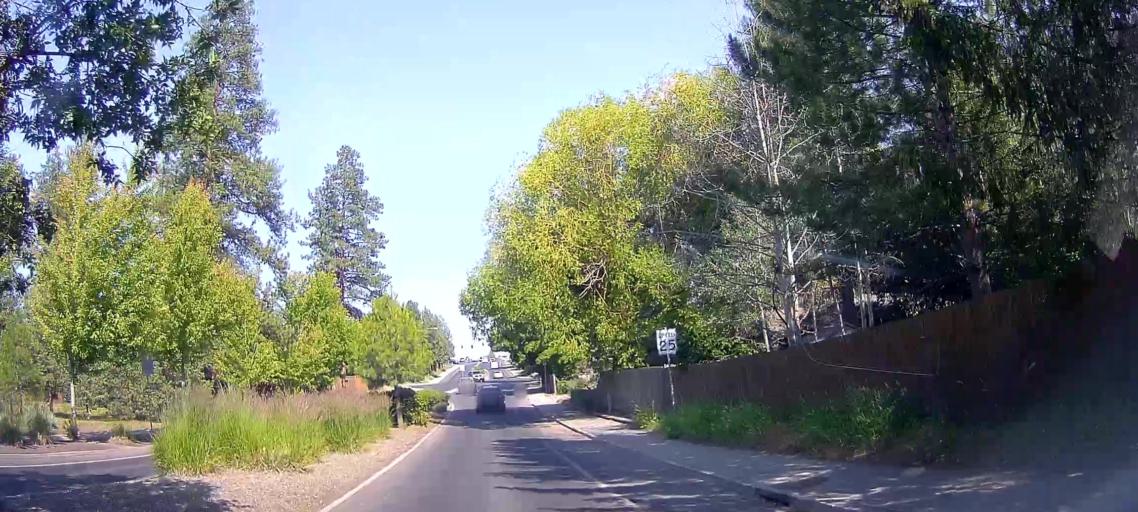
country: US
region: Oregon
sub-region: Deschutes County
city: Bend
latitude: 44.0397
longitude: -121.3133
